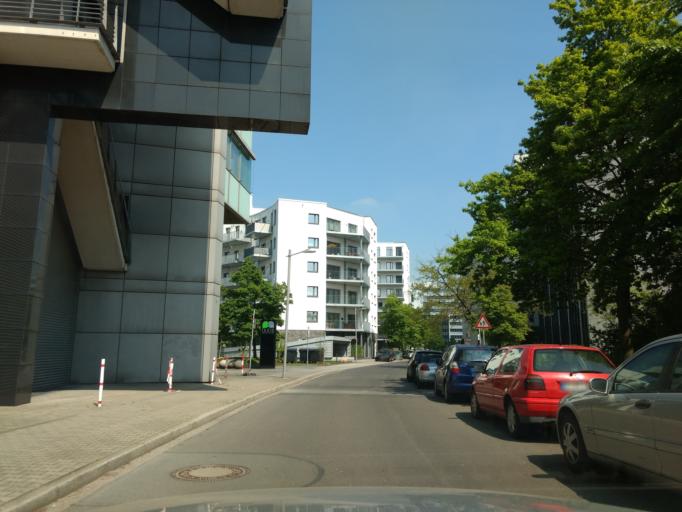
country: DE
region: North Rhine-Westphalia
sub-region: Regierungsbezirk Dusseldorf
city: Dusseldorf
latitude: 51.2327
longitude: 6.8202
